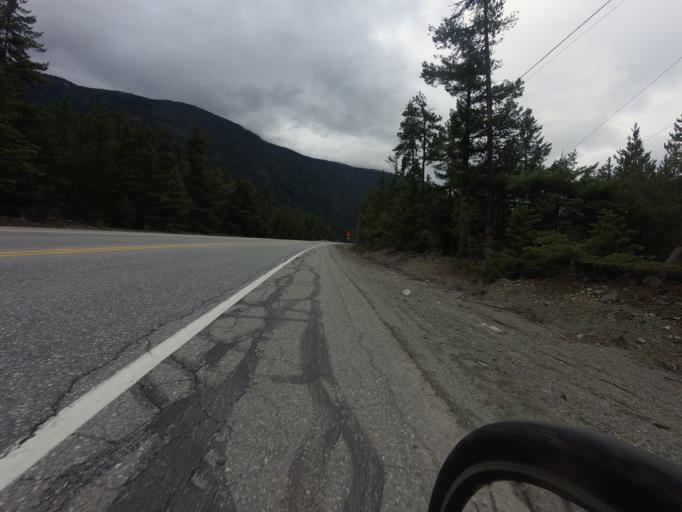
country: CA
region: British Columbia
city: Pemberton
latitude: 50.2673
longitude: -122.8676
